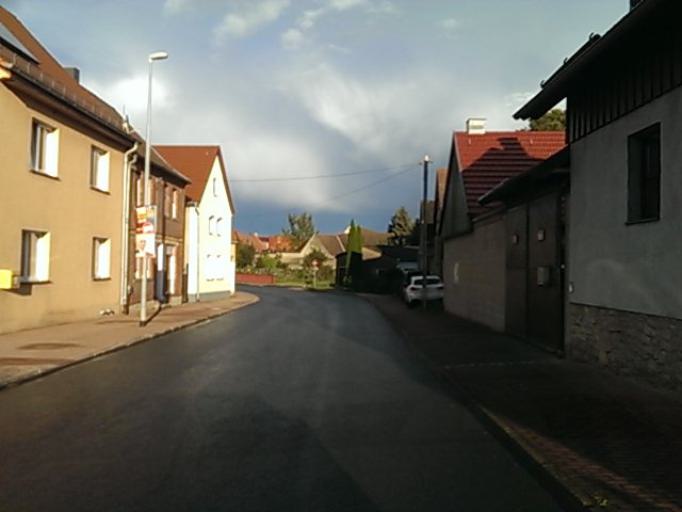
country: DE
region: Thuringia
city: Ostramondra
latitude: 51.1984
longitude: 11.3252
